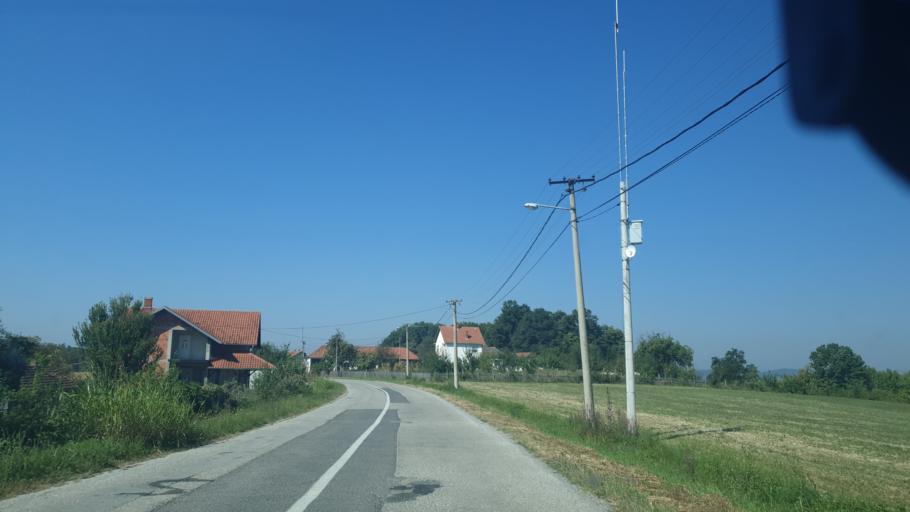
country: RS
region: Central Serbia
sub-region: Kolubarski Okrug
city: Lajkovac
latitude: 44.3085
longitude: 20.1562
